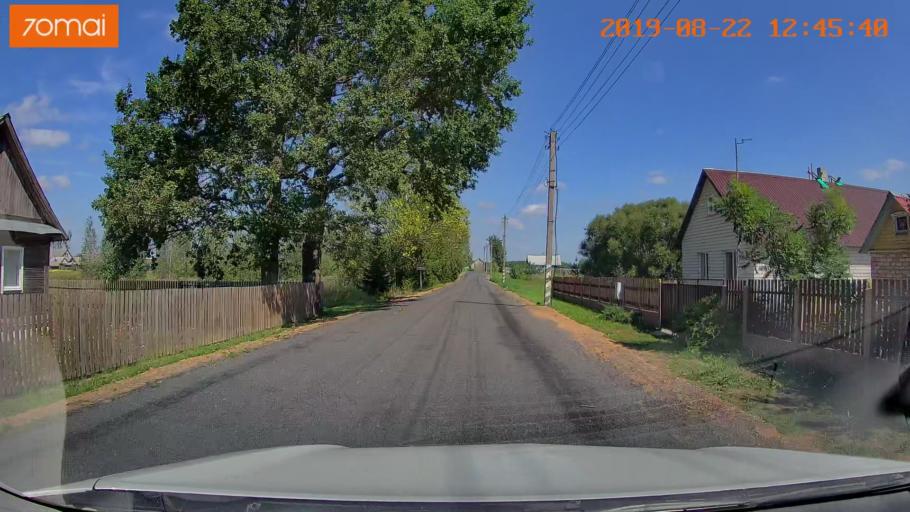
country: BY
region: Minsk
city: Prawdzinski
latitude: 53.4594
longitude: 27.6214
